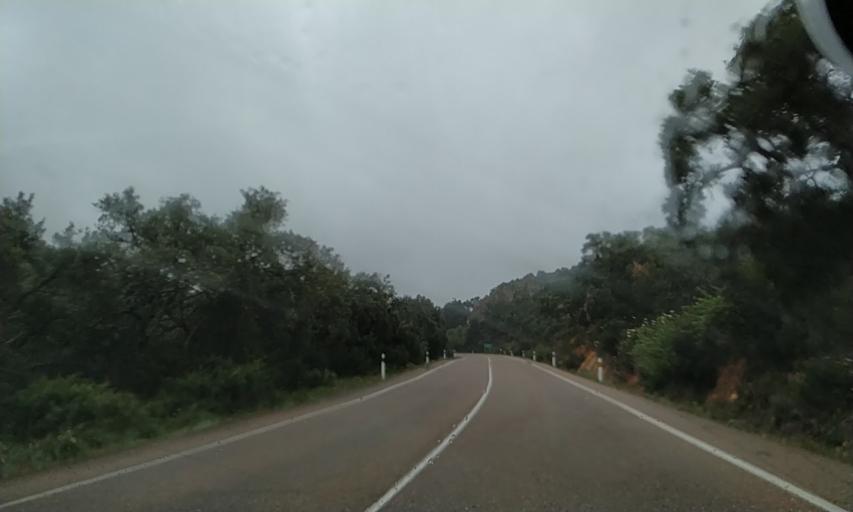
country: ES
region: Extremadura
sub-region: Provincia de Badajoz
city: Puebla de Obando
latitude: 39.1878
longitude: -6.5996
